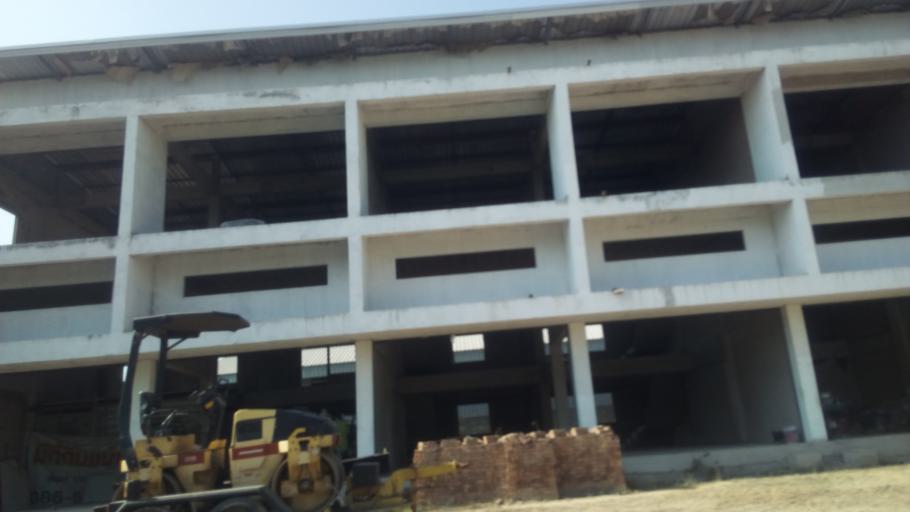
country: TH
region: Nonthaburi
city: Bang Yai
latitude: 13.8793
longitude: 100.3033
